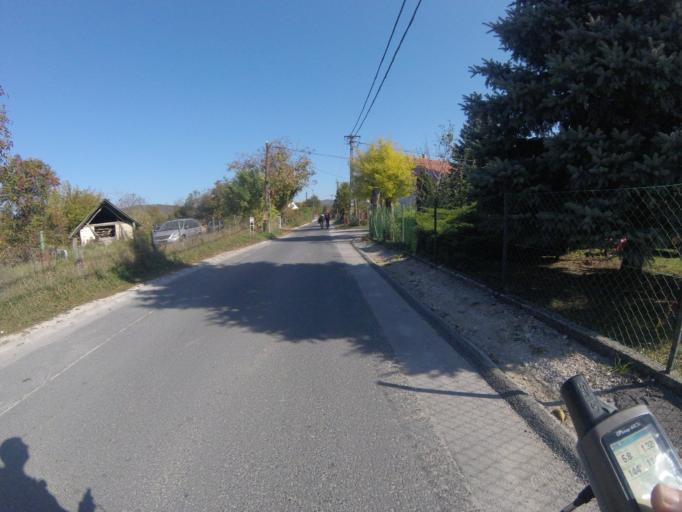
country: HU
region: Zala
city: Gyenesdias
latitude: 46.7807
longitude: 17.2807
